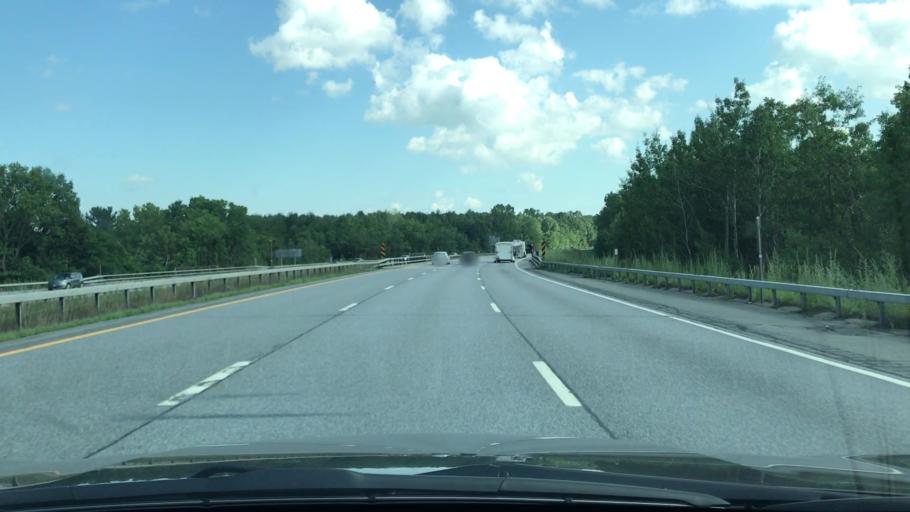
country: US
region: New York
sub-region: Warren County
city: Glens Falls North
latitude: 43.3182
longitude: -73.6763
